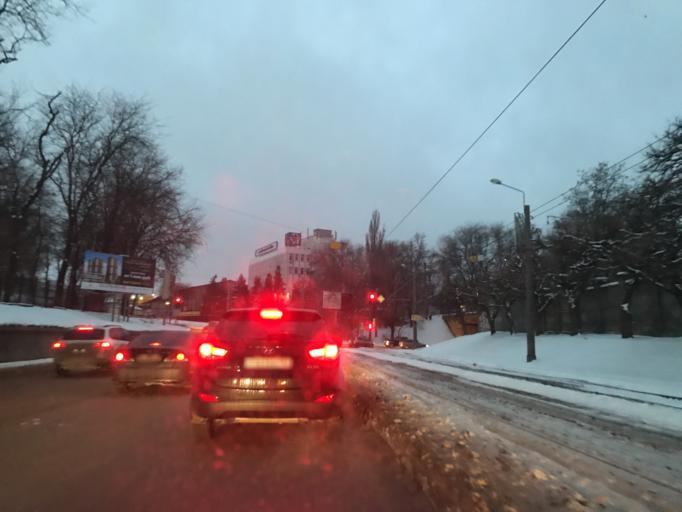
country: RU
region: Rostov
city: Rostov-na-Donu
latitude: 47.2440
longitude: 39.7522
